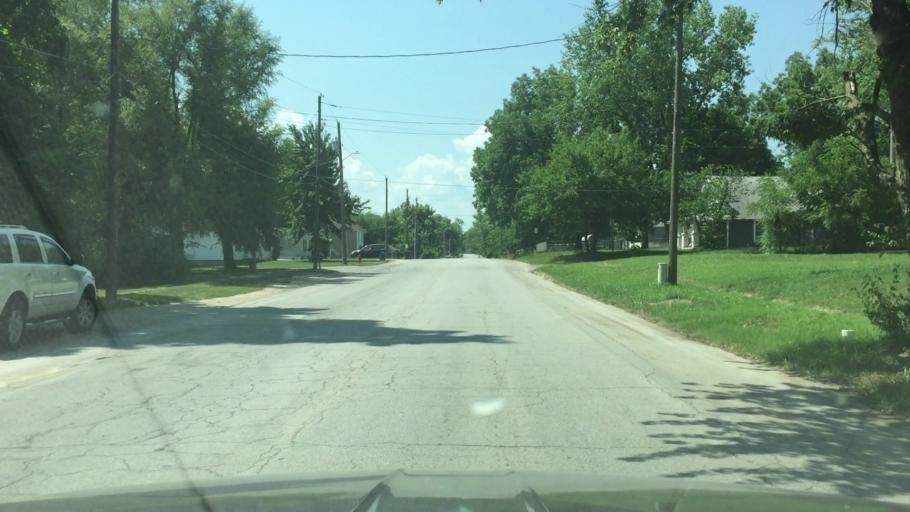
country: US
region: Missouri
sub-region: Miller County
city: Eldon
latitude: 38.3446
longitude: -92.5865
